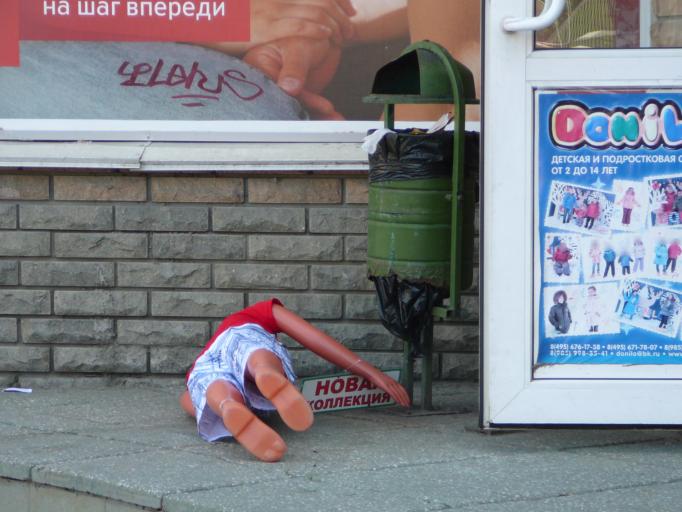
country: RU
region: Moskovskaya
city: Pavshino
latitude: 55.8161
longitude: 37.3408
